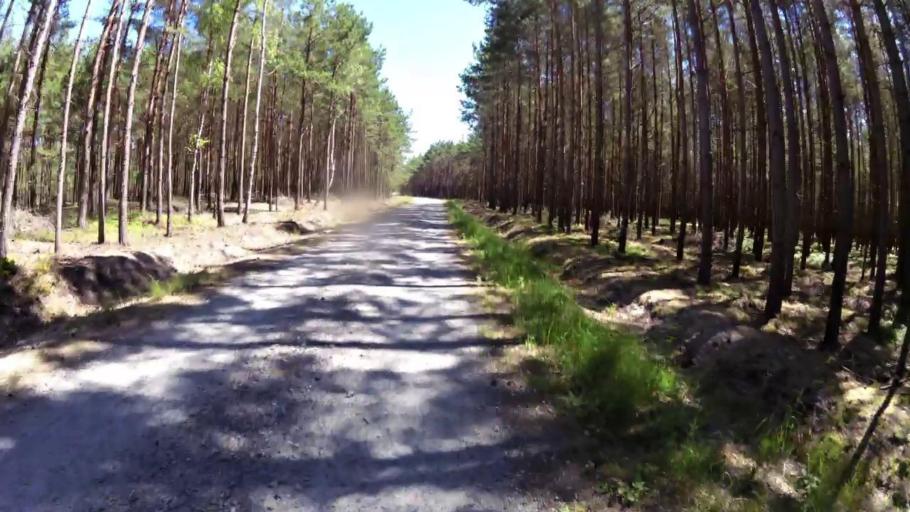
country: PL
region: West Pomeranian Voivodeship
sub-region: Powiat gryficki
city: Cerkwica
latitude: 54.0995
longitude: 15.1597
